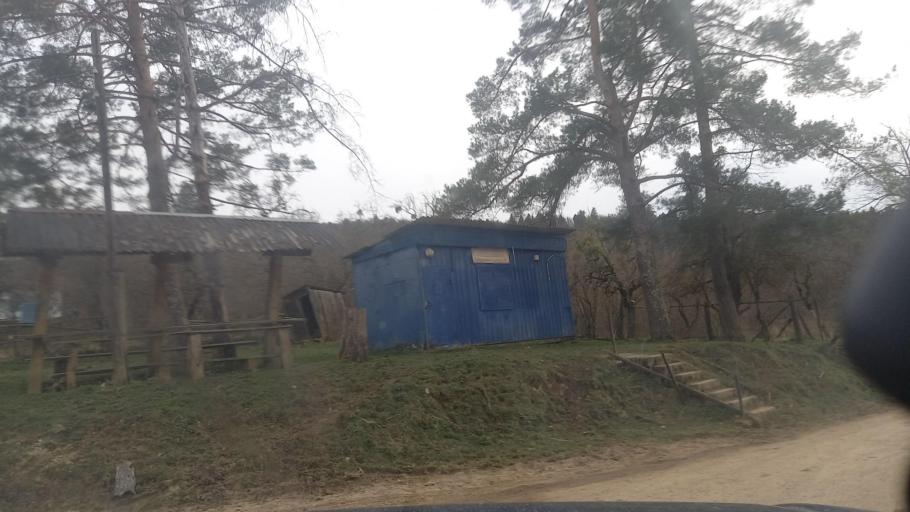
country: RU
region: Adygeya
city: Kamennomostskiy
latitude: 44.2039
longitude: 40.0028
